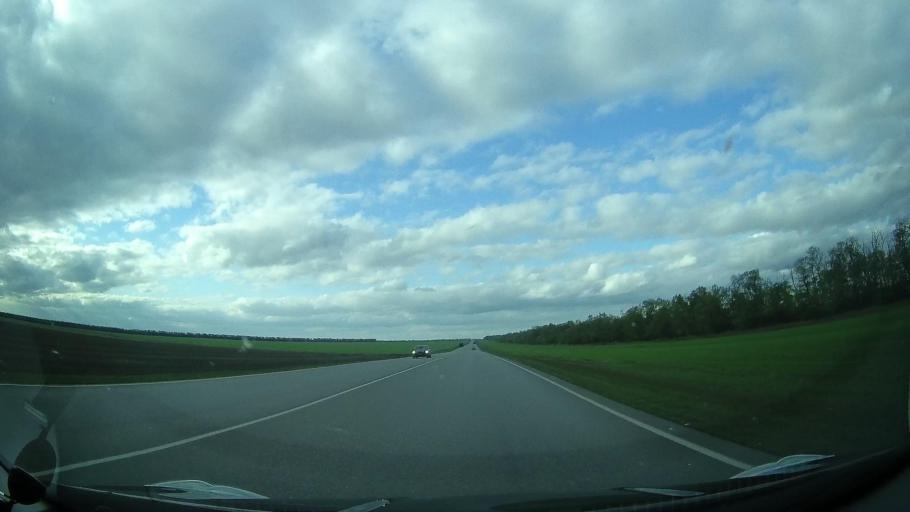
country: RU
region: Rostov
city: Kagal'nitskaya
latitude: 46.9023
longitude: 40.1216
